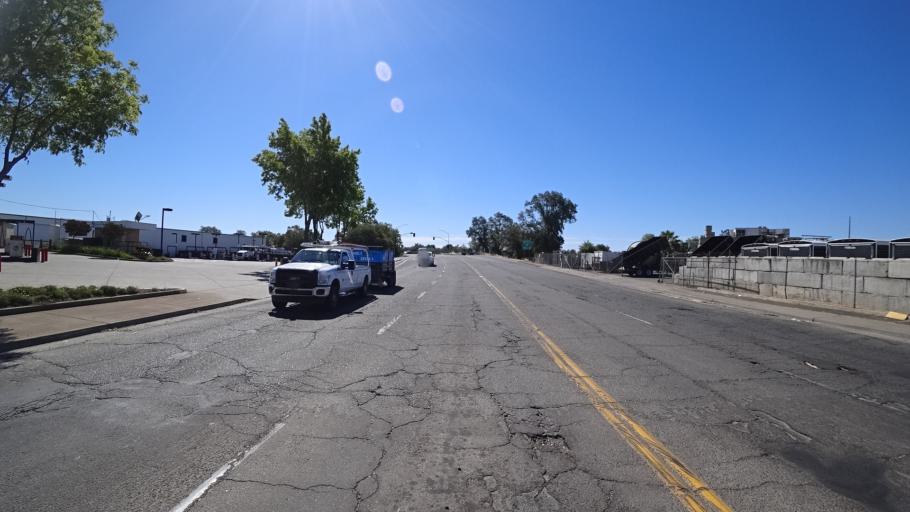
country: US
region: California
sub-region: Sacramento County
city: Arden-Arcade
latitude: 38.6415
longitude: -121.4012
